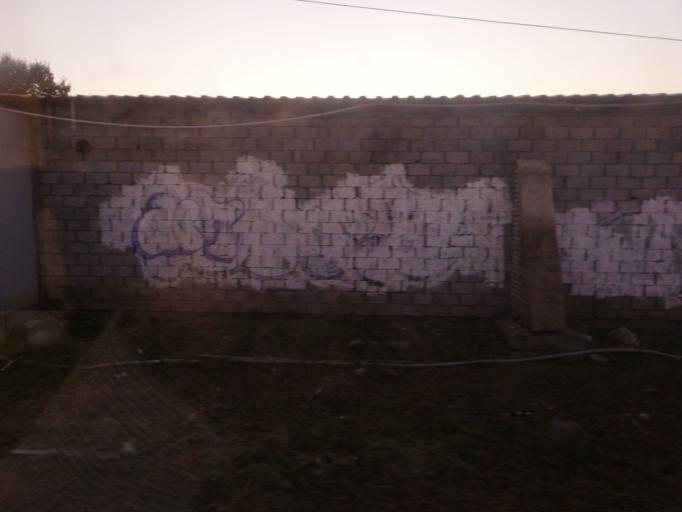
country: RU
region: Moscow
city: Mar'ina Roshcha
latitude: 55.7957
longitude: 37.5914
